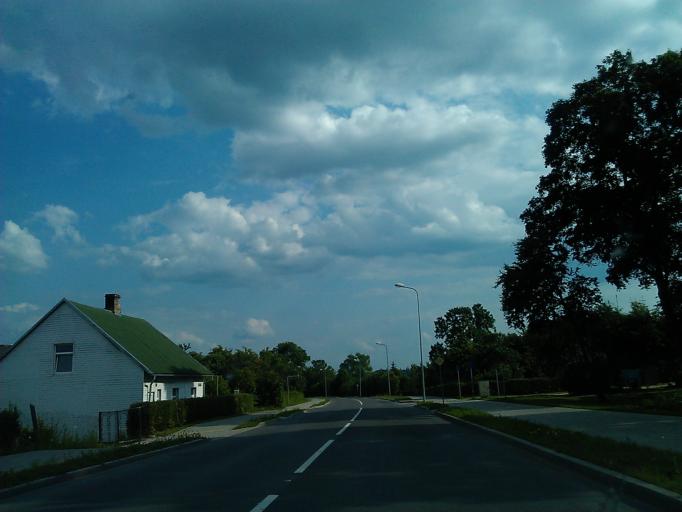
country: LV
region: Aizpute
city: Aizpute
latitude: 56.7137
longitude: 21.6162
